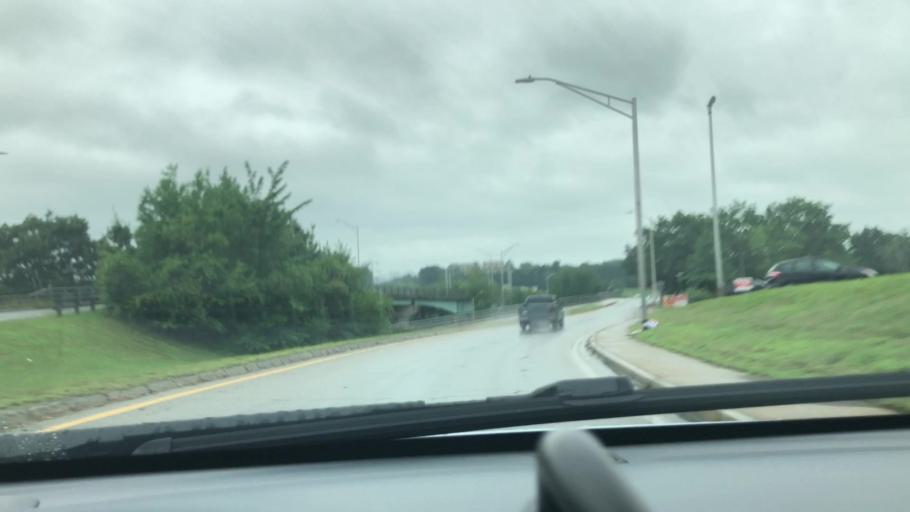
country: US
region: New Hampshire
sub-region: Hillsborough County
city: Manchester
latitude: 43.0030
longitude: -71.4667
